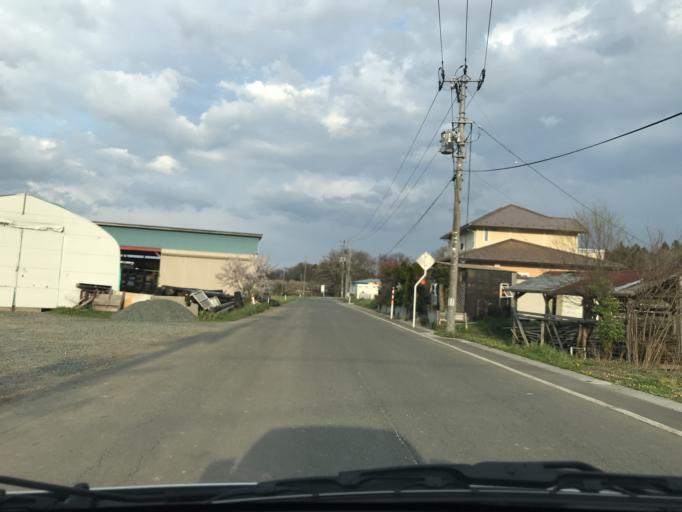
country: JP
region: Iwate
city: Mizusawa
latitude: 39.1064
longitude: 141.1130
